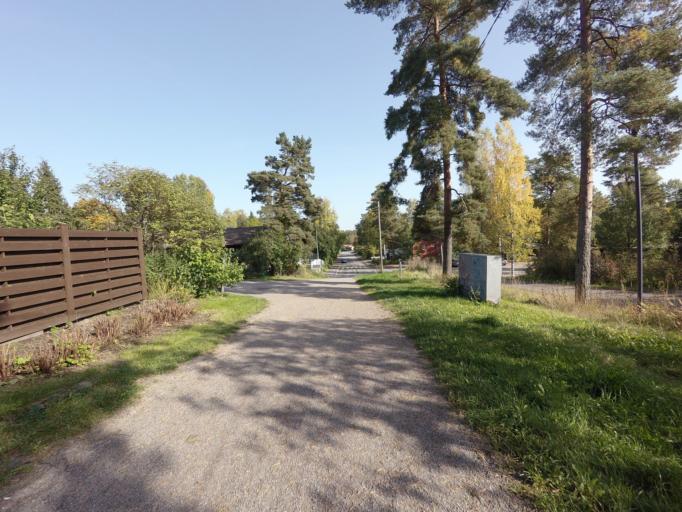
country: FI
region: Uusimaa
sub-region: Helsinki
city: Espoo
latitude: 60.1782
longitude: 24.6523
